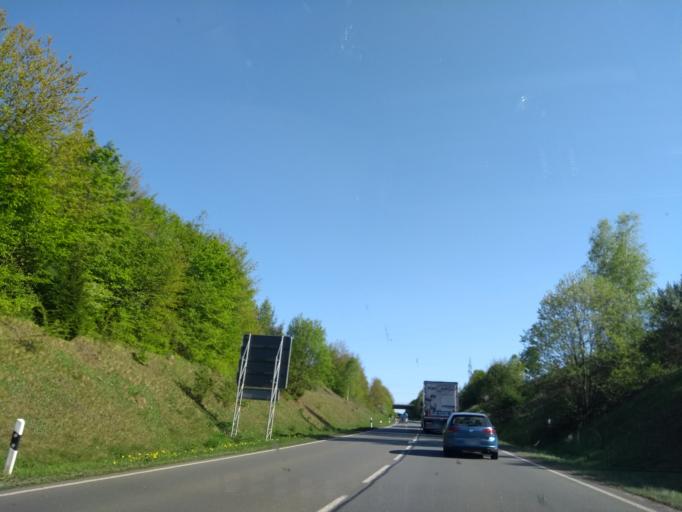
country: DE
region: Hesse
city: Frankenberg
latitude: 51.0687
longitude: 8.8138
